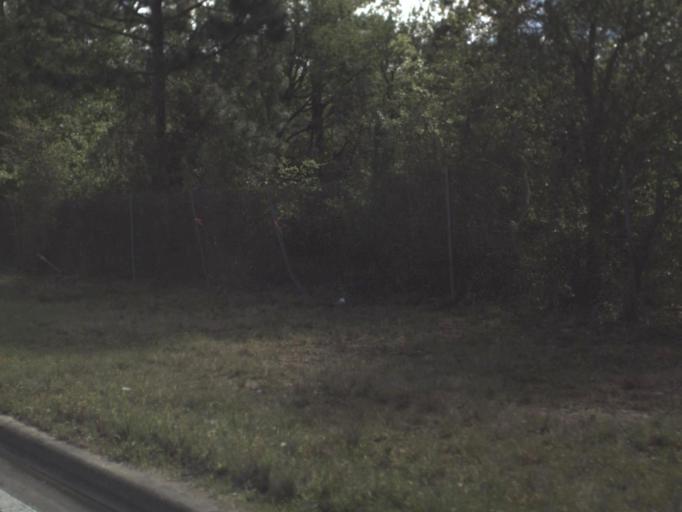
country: US
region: Florida
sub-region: Escambia County
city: West Pensacola
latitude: 30.4333
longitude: -87.2696
